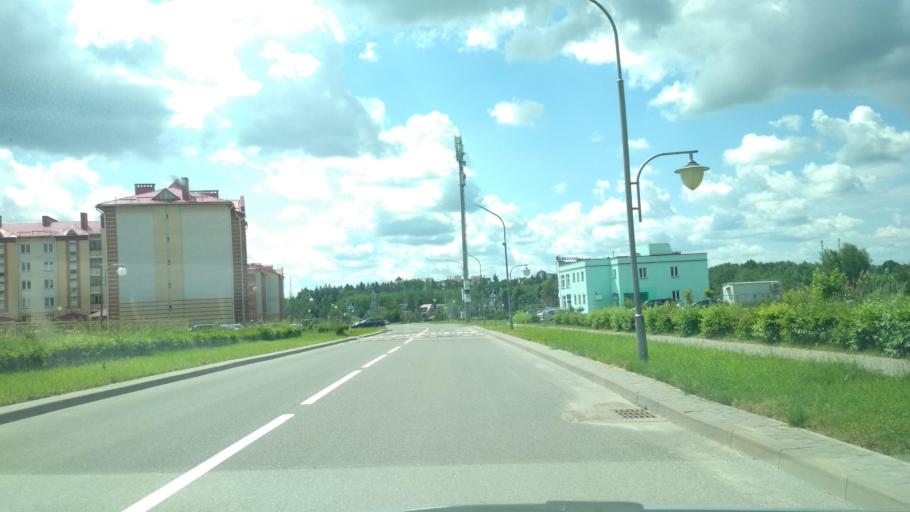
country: BY
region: Grodnenskaya
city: Astravyets
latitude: 54.6162
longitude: 25.9763
